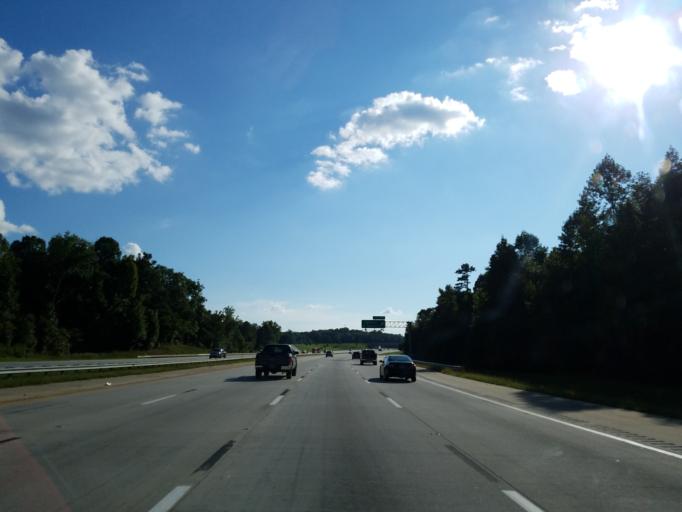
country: US
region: North Carolina
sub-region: Rowan County
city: East Spencer
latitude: 35.6821
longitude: -80.4087
